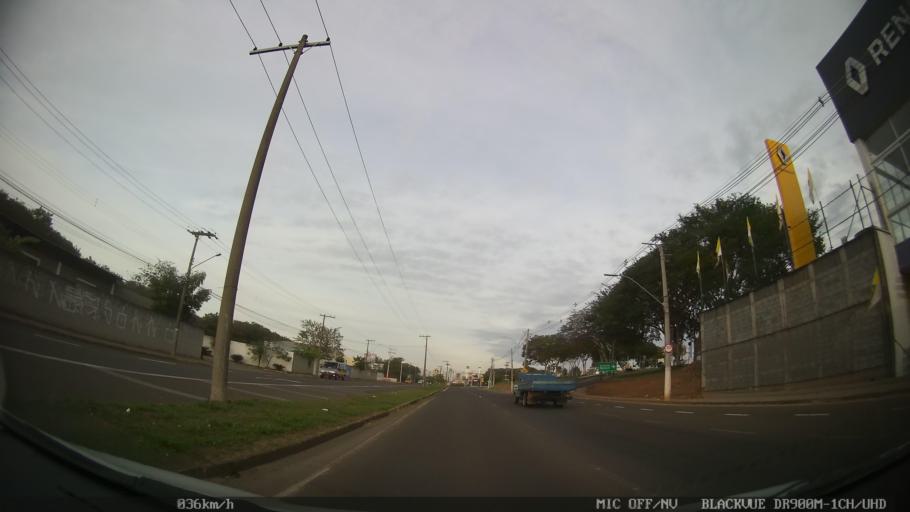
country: BR
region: Sao Paulo
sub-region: Limeira
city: Limeira
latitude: -22.5865
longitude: -47.3927
